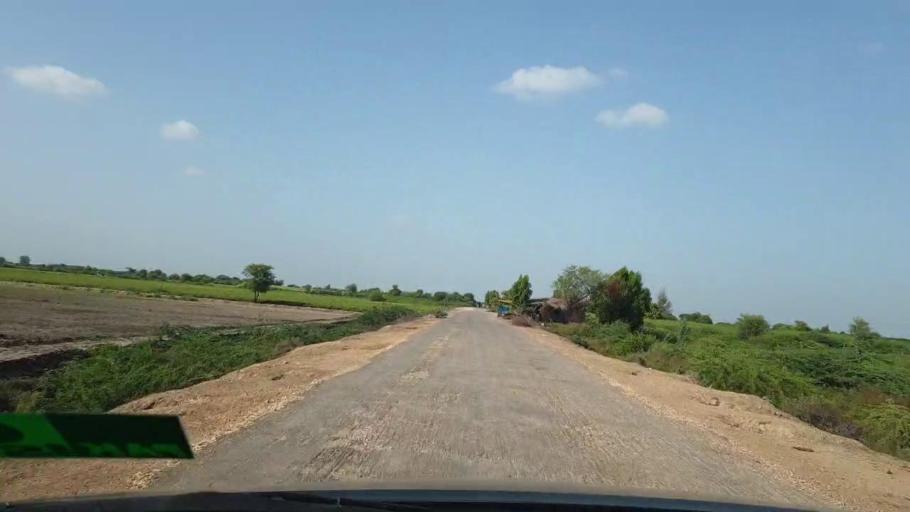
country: PK
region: Sindh
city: Tando Bago
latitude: 24.7077
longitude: 69.1922
